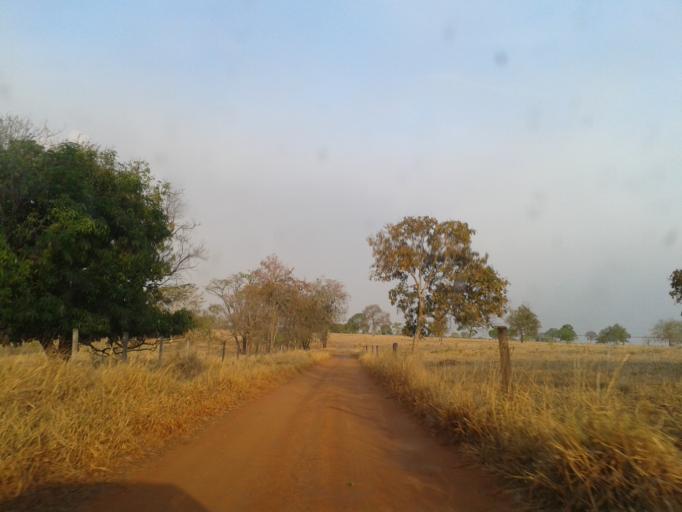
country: BR
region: Minas Gerais
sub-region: Capinopolis
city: Capinopolis
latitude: -18.8051
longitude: -49.7538
